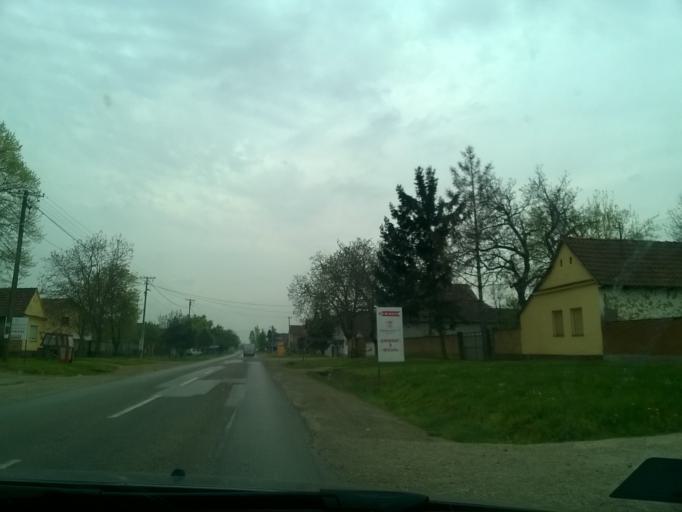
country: RS
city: Hrtkovci
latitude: 44.8719
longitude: 19.7699
